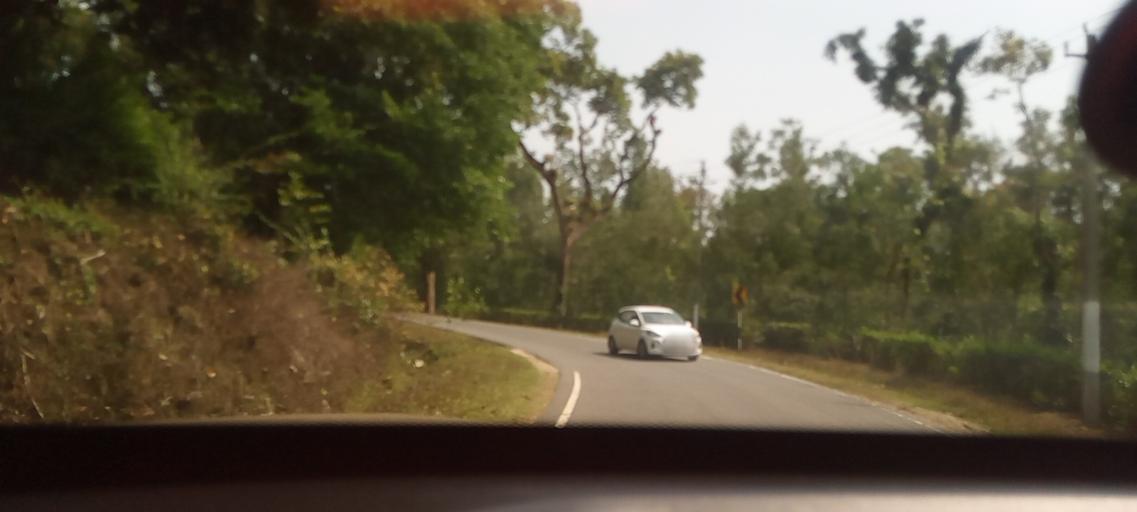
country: IN
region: Karnataka
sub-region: Chikmagalur
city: Mudigere
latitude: 13.2556
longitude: 75.6356
